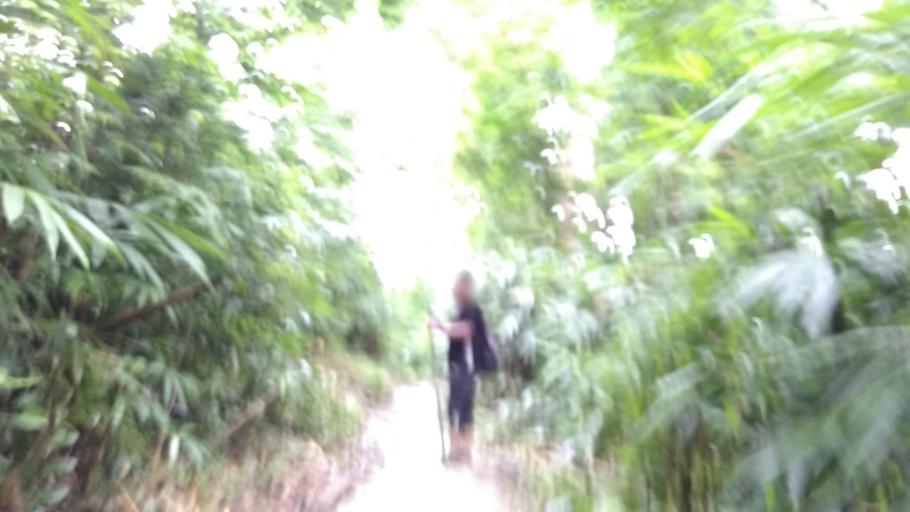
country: IN
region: Tripura
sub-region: Dhalai
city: Kamalpur
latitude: 24.1707
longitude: 91.8977
